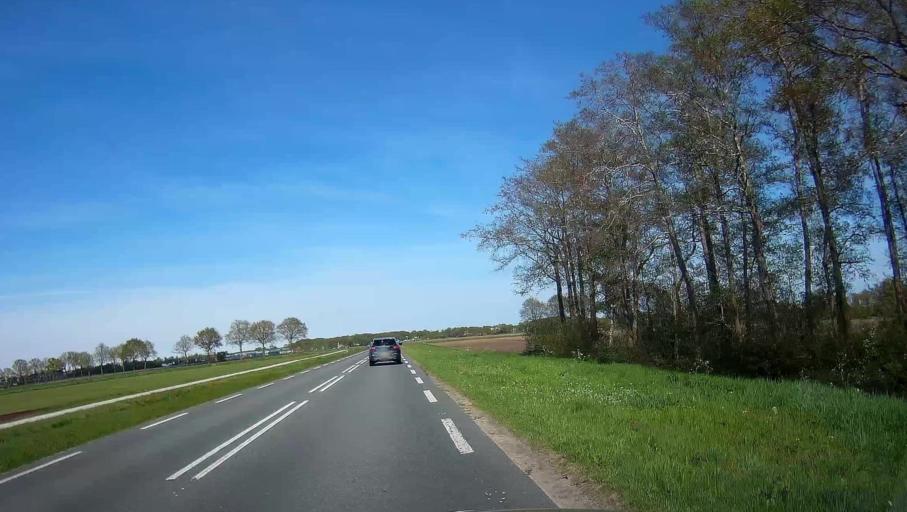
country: NL
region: Drenthe
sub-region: Gemeente Borger-Odoorn
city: Borger
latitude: 52.9160
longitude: 6.7656
